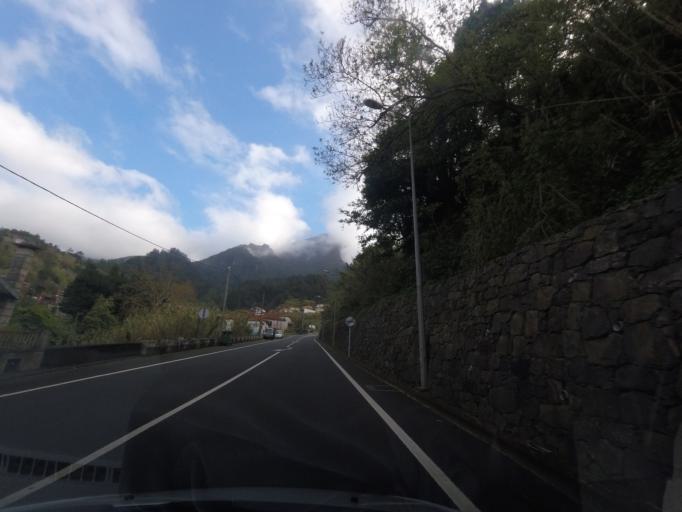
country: PT
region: Madeira
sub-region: Sao Vicente
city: Sao Vicente
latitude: 32.7789
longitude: -17.0333
